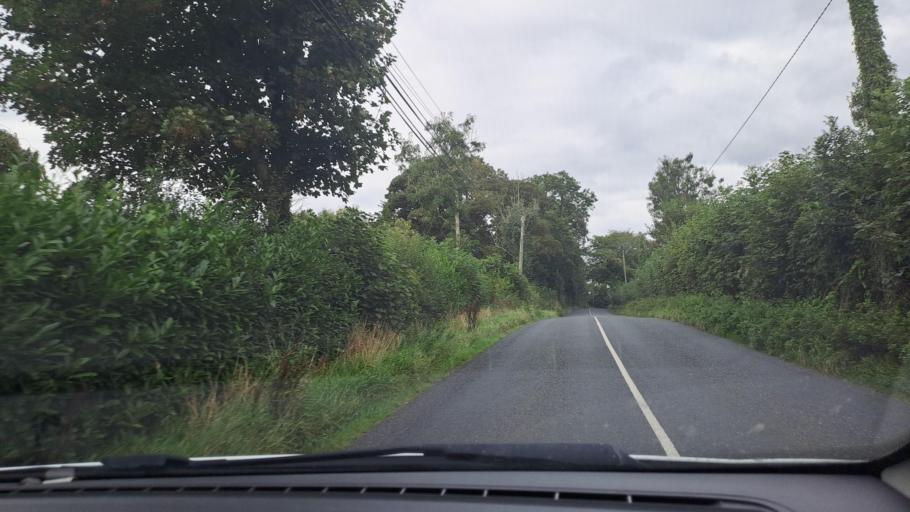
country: IE
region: Ulster
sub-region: An Cabhan
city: Bailieborough
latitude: 54.0052
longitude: -6.9163
